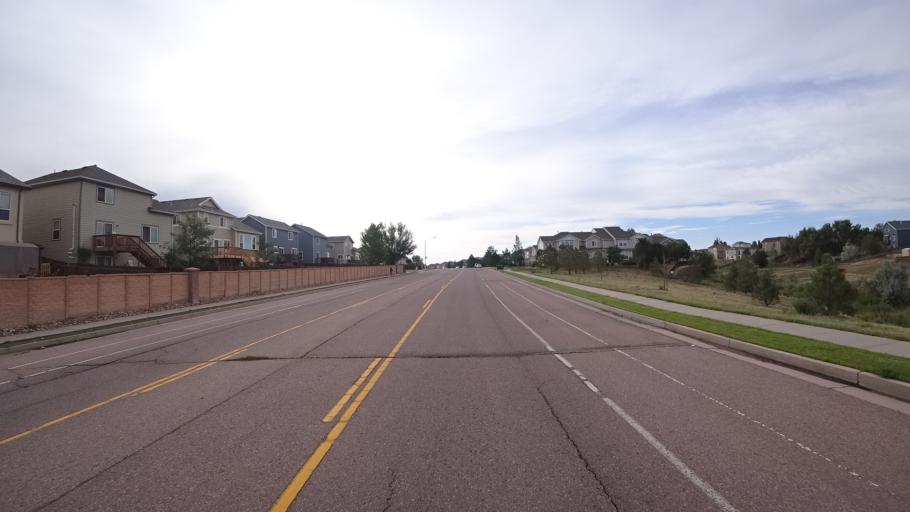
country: US
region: Colorado
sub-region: El Paso County
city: Fountain
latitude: 38.7153
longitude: -104.6934
